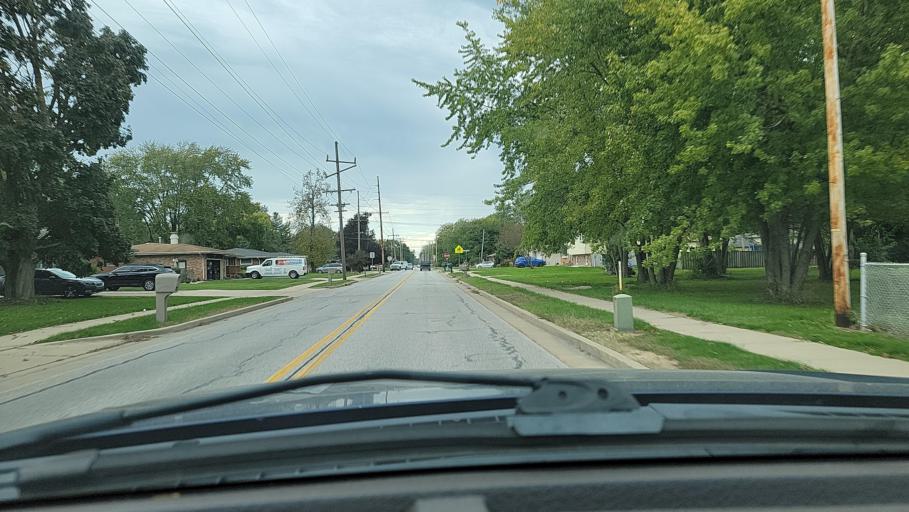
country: US
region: Indiana
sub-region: Porter County
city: Portage
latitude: 41.5651
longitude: -87.2008
